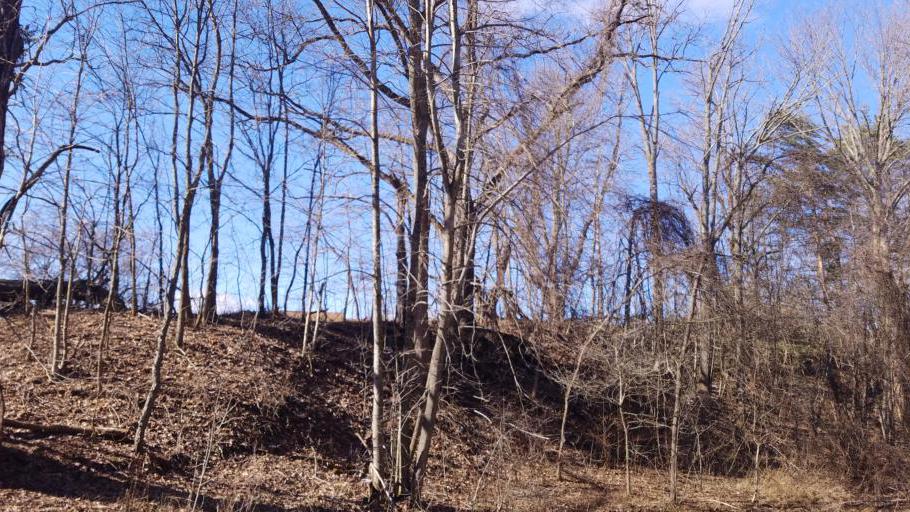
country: US
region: Ohio
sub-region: Richland County
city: Lexington
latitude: 40.6657
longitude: -82.6450
